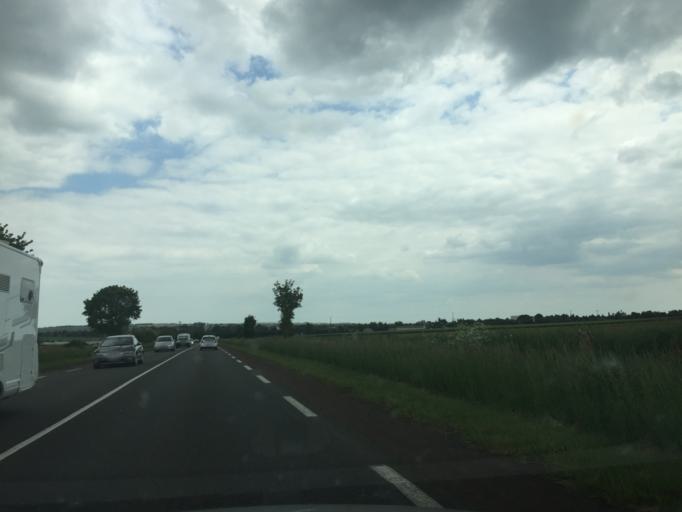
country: FR
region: Pays de la Loire
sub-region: Departement de la Vendee
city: Benet
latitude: 46.3797
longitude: -0.6035
